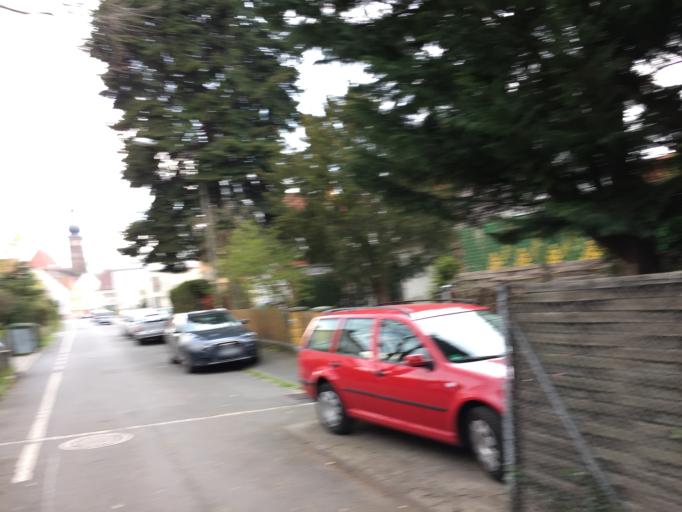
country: DE
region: Bavaria
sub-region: Regierungsbezirk Mittelfranken
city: Erlangen
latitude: 49.5686
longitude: 10.9632
